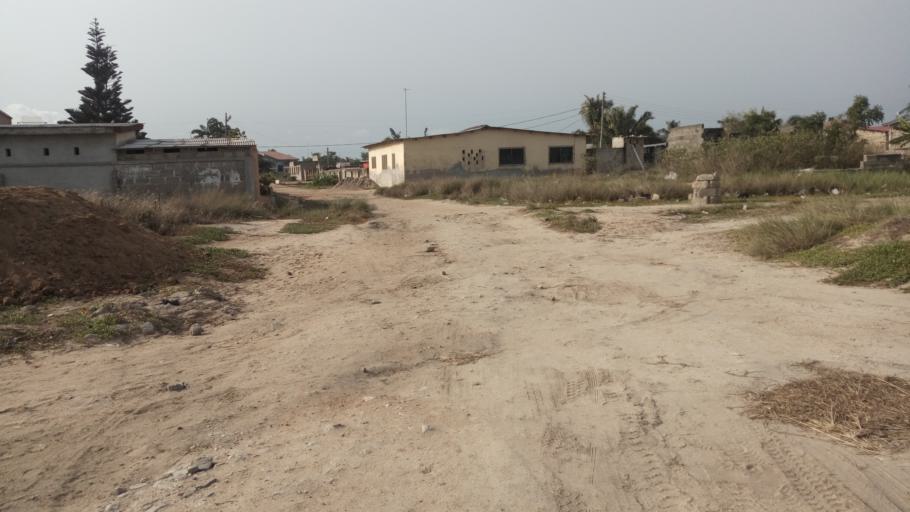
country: GH
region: Central
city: Winneba
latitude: 5.3484
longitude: -0.6337
